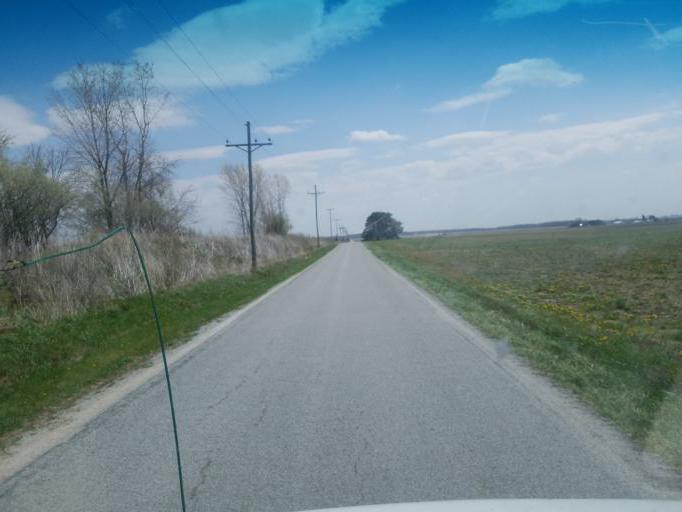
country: US
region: Ohio
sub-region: Hardin County
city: Forest
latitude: 40.7598
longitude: -83.5291
